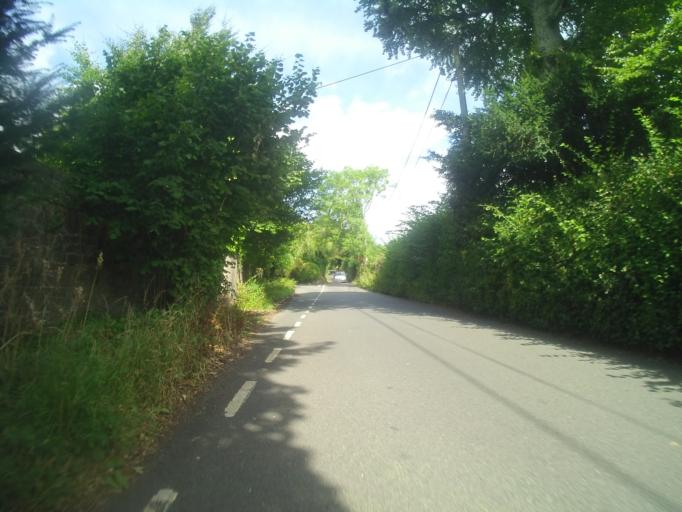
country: GB
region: England
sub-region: Devon
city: Totnes
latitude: 50.4377
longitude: -3.7022
